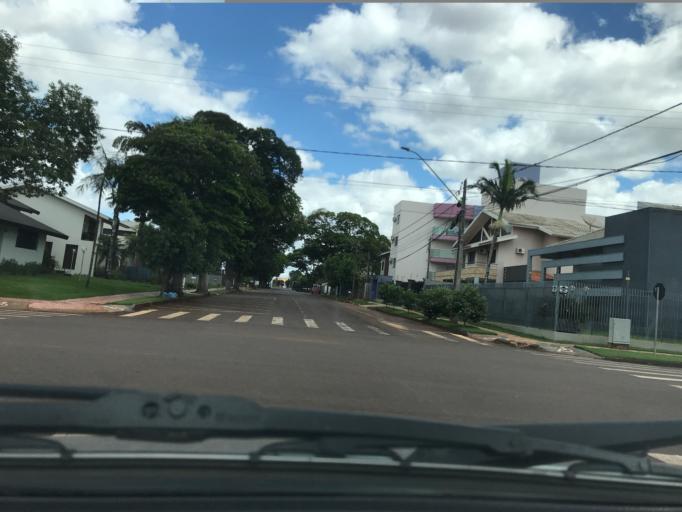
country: BR
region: Parana
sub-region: Palotina
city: Palotina
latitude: -24.2886
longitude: -53.8395
